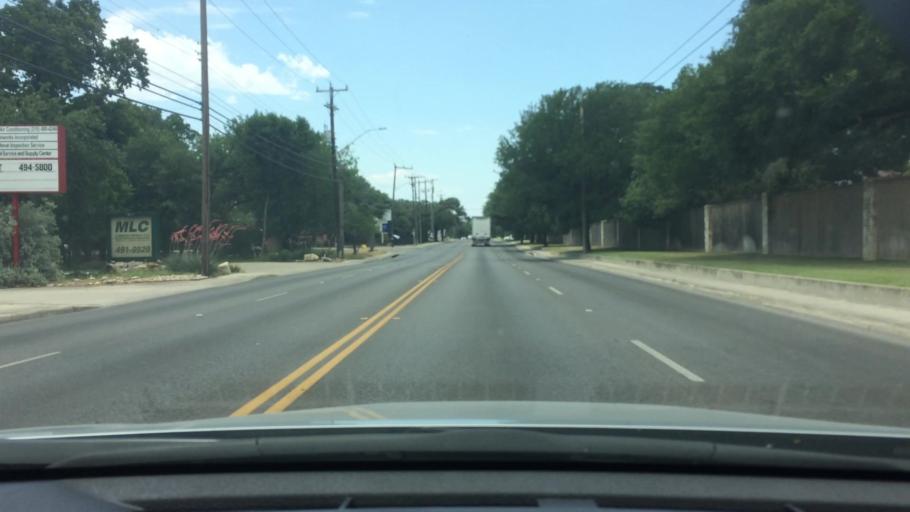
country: US
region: Texas
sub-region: Bexar County
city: Hollywood Park
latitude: 29.5749
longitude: -98.4454
